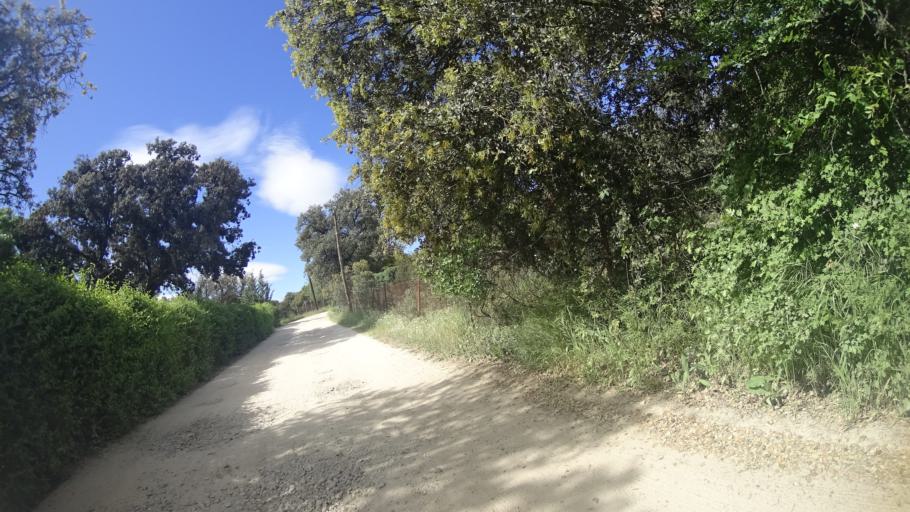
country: ES
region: Madrid
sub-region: Provincia de Madrid
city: Brunete
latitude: 40.4178
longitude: -3.9497
